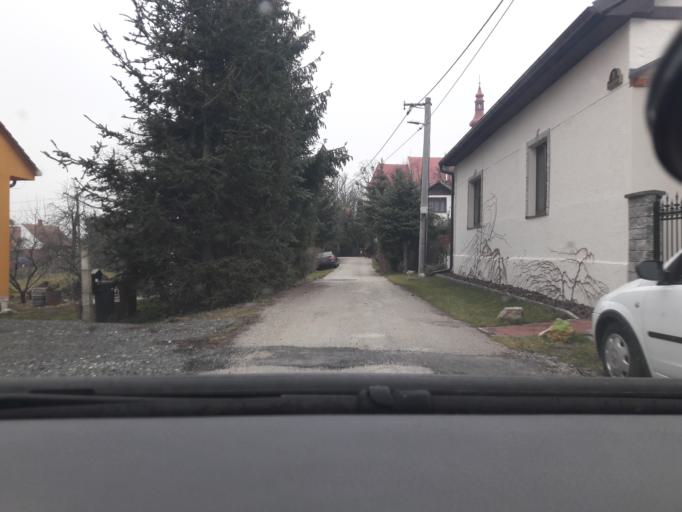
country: SK
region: Trnavsky
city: Smolenice
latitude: 48.5110
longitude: 17.4334
